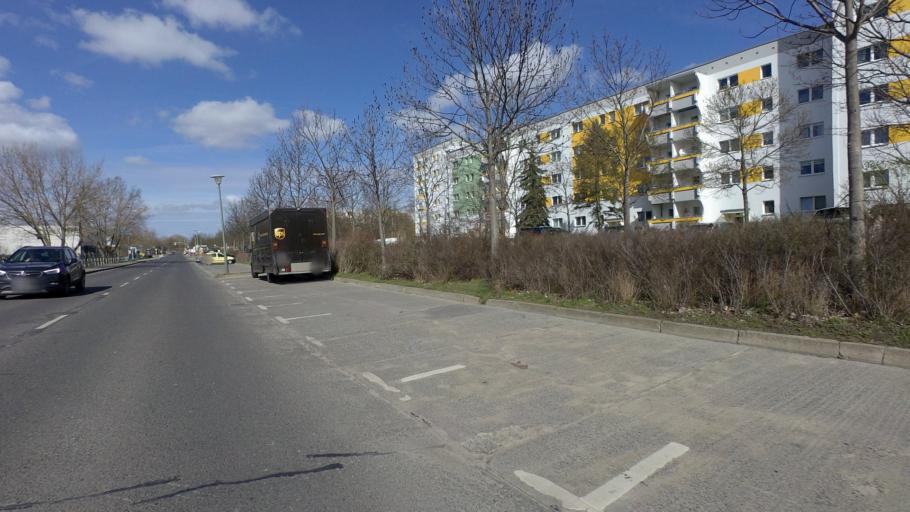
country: DE
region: Berlin
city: Neu-Hohenschoenhausen
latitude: 52.5720
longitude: 13.5067
